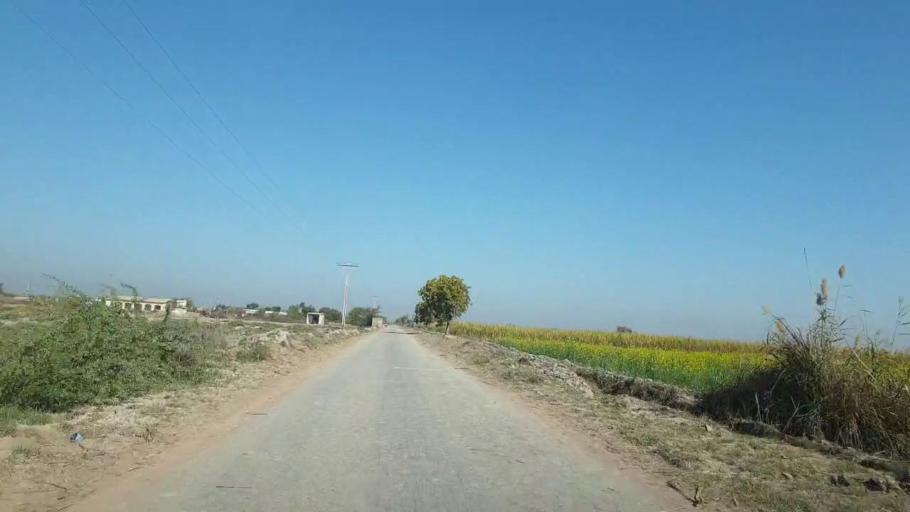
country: PK
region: Sindh
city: Mirpur Khas
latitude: 25.5951
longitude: 69.0452
